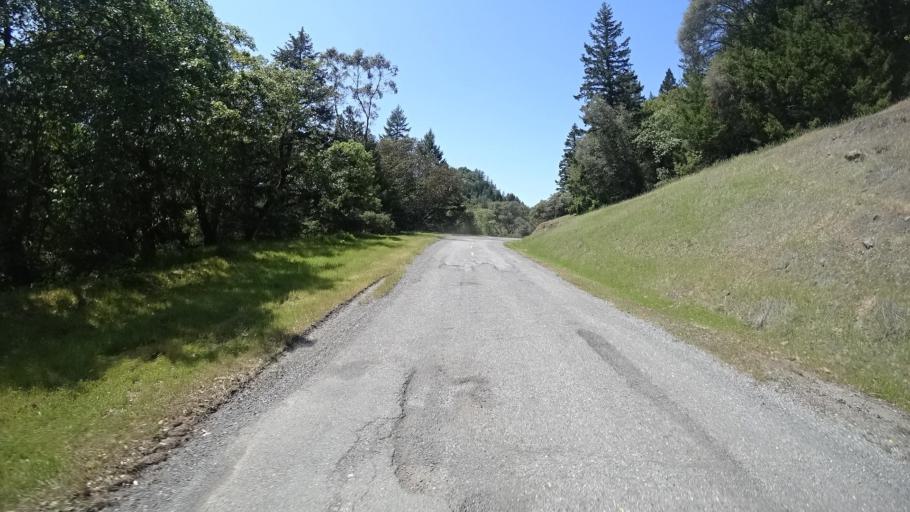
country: US
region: California
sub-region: Humboldt County
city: Redway
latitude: 40.2281
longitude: -123.6442
